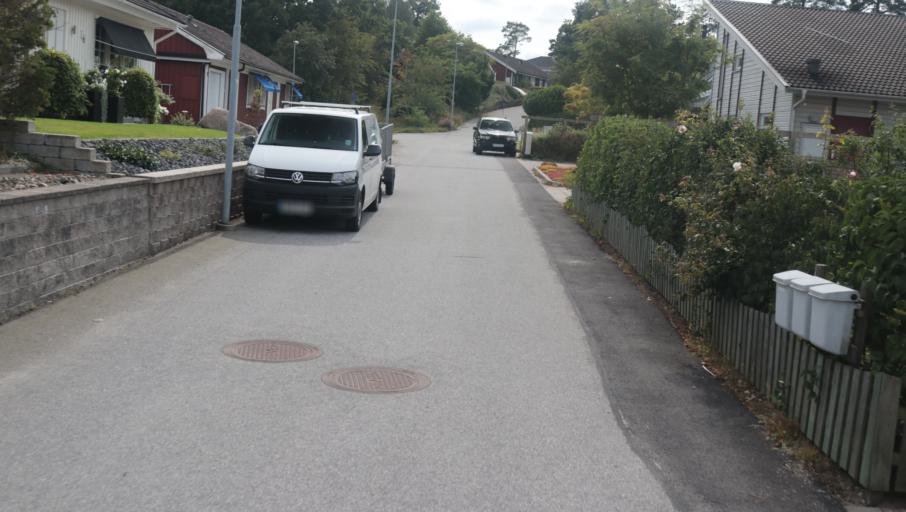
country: SE
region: Blekinge
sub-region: Karlshamns Kommun
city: Karlshamn
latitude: 56.2068
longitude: 14.8616
